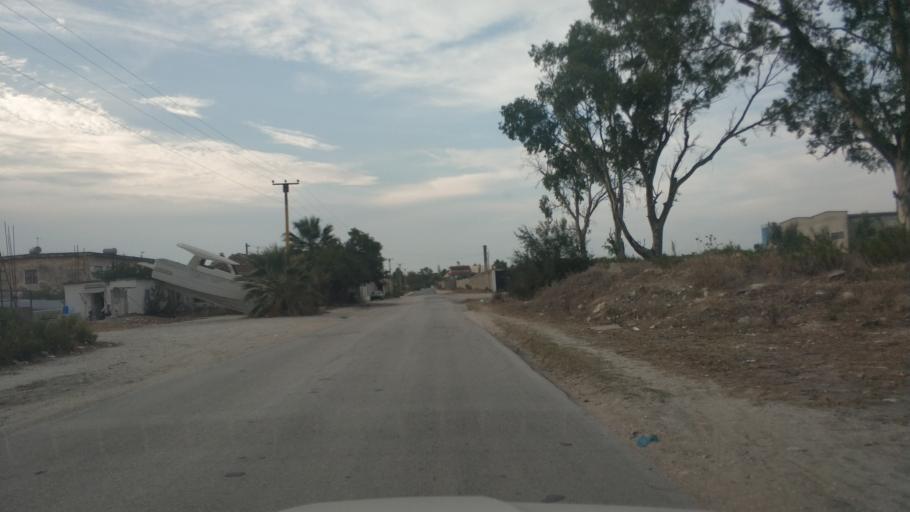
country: AL
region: Vlore
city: Vlore
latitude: 40.4736
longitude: 19.4561
